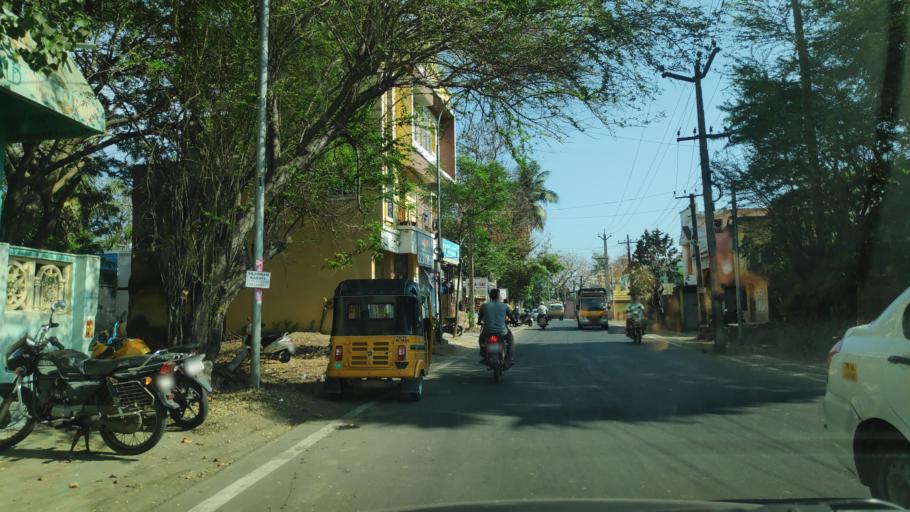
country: IN
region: Tamil Nadu
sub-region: Thiruvallur
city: Ambattur
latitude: 13.1192
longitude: 80.1689
